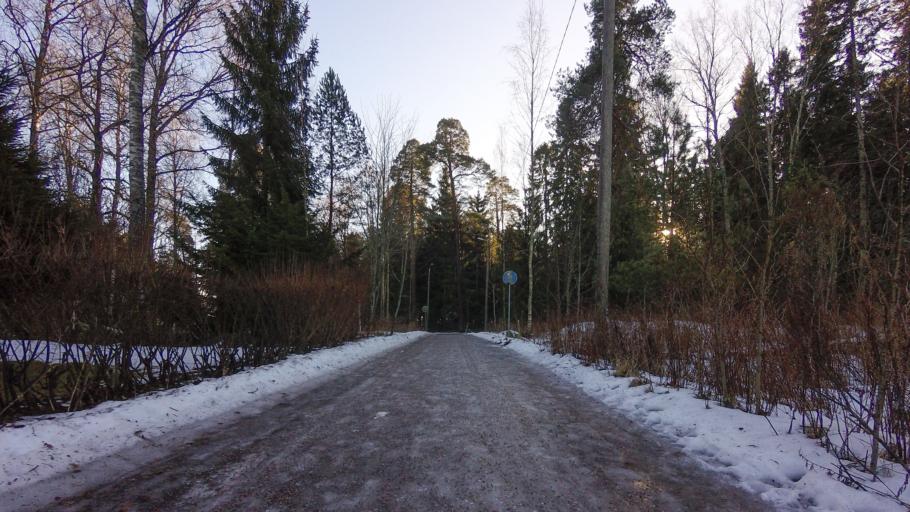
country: FI
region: Uusimaa
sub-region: Helsinki
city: Vantaa
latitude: 60.1793
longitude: 25.0643
